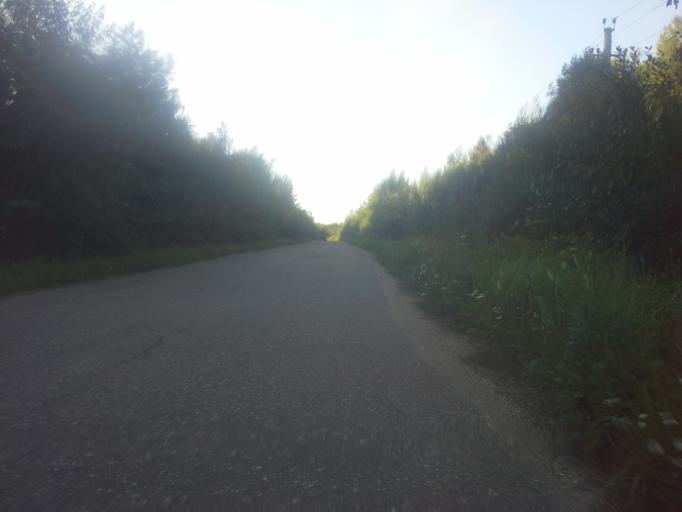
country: RU
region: Moskovskaya
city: Kievskij
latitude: 55.3866
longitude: 36.9043
